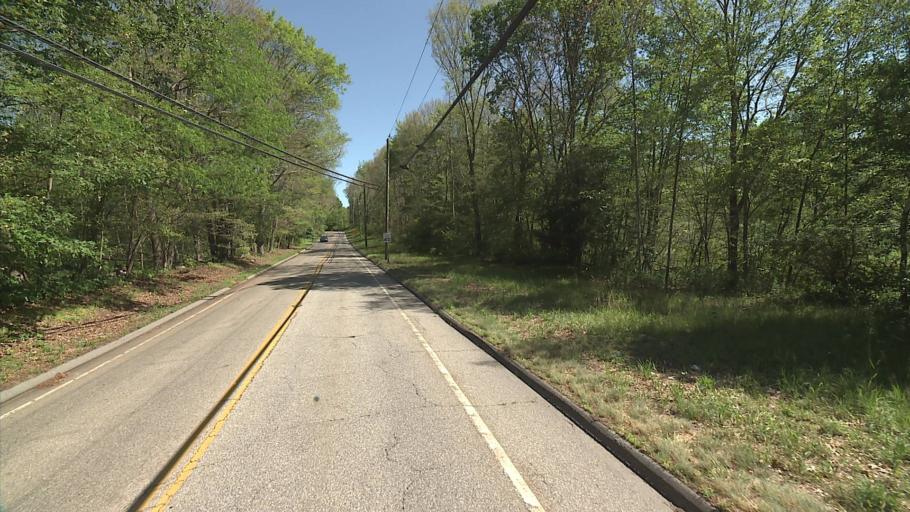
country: US
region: Connecticut
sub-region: New London County
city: Colchester
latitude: 41.5835
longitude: -72.3101
